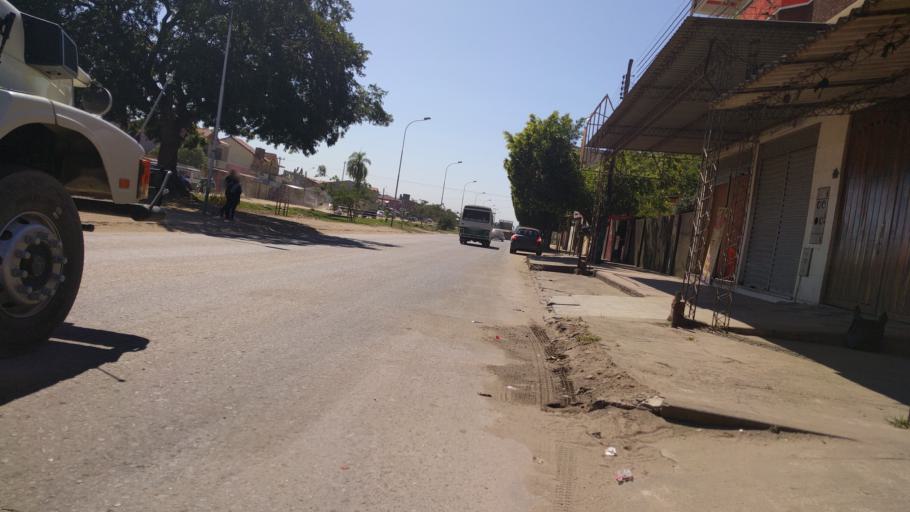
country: BO
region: Santa Cruz
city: Santa Cruz de la Sierra
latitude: -17.8200
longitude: -63.2284
